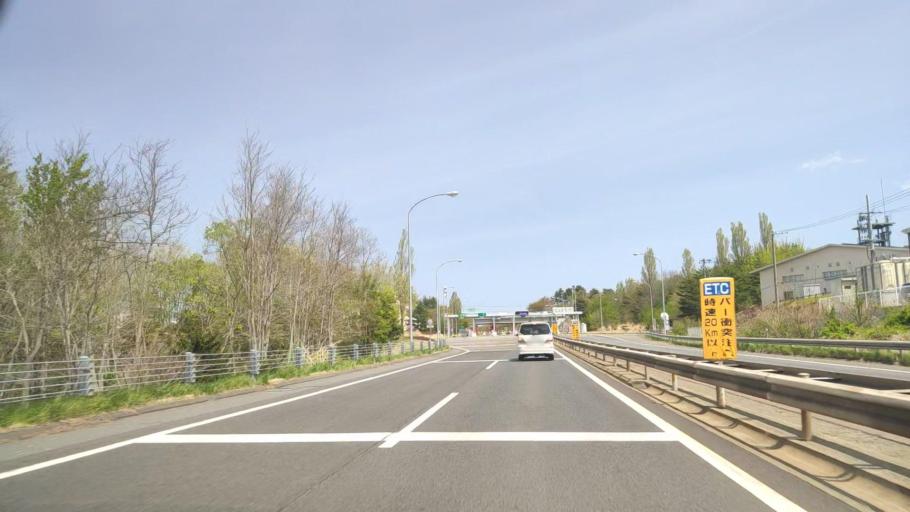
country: JP
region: Aomori
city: Hachinohe
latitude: 40.4848
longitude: 141.4616
